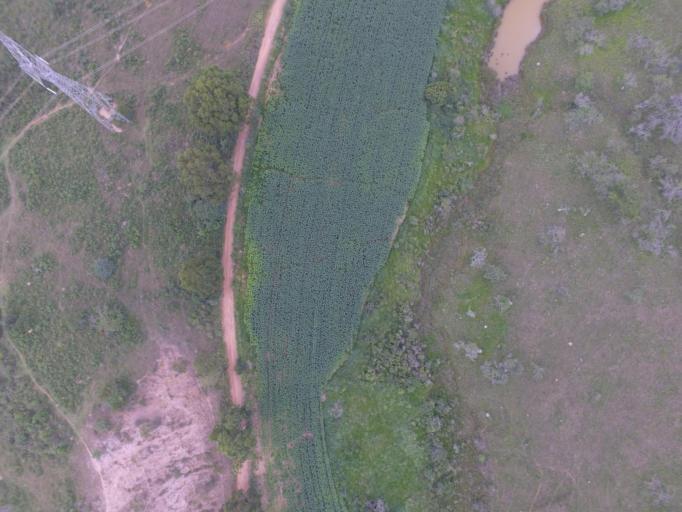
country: BR
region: Minas Gerais
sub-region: Tiradentes
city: Tiradentes
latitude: -21.0453
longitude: -44.0850
